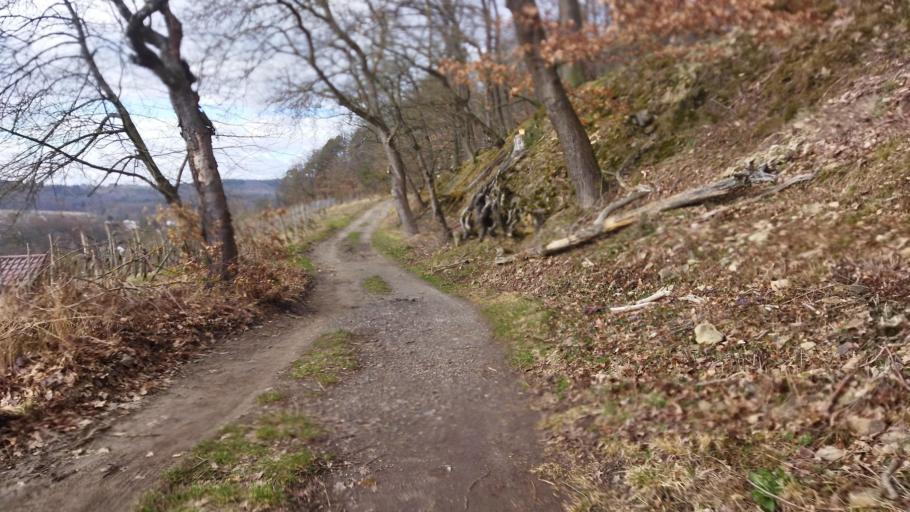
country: DE
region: Baden-Wuerttemberg
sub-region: Regierungsbezirk Stuttgart
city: Freudental
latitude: 49.0081
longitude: 9.0728
